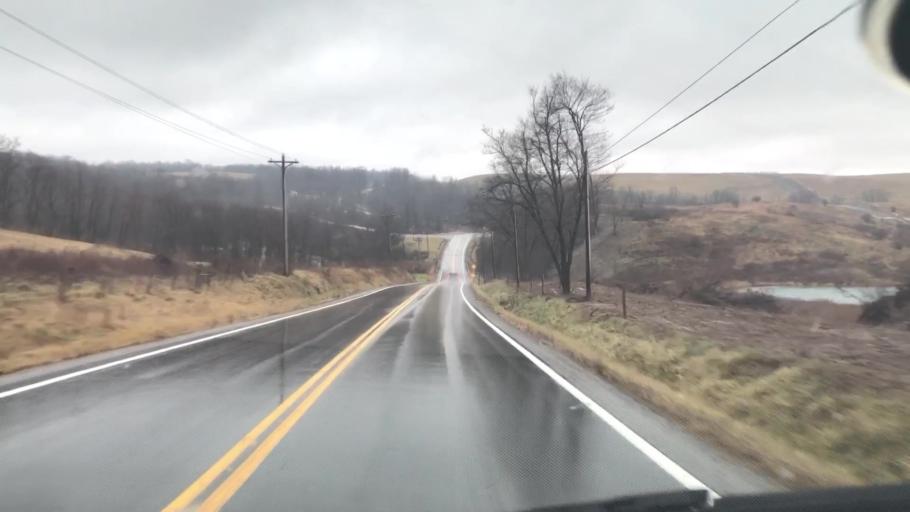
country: US
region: Ohio
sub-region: Harrison County
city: Cadiz
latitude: 40.2236
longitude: -81.0028
